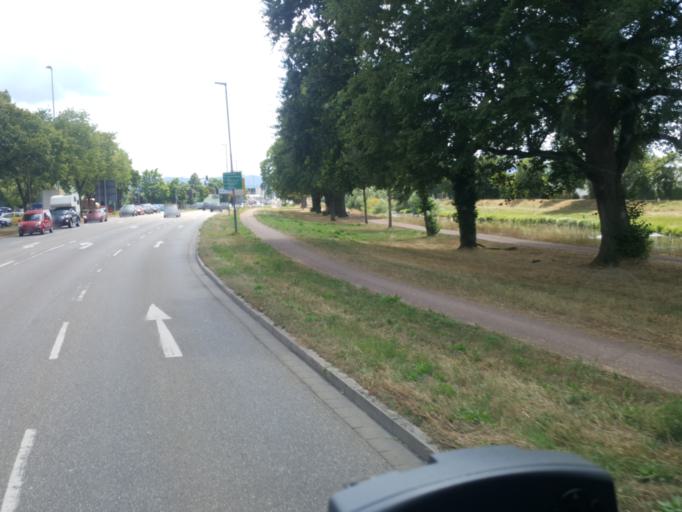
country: DE
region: Baden-Wuerttemberg
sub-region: Freiburg Region
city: Emmendingen
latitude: 48.1167
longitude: 7.8481
